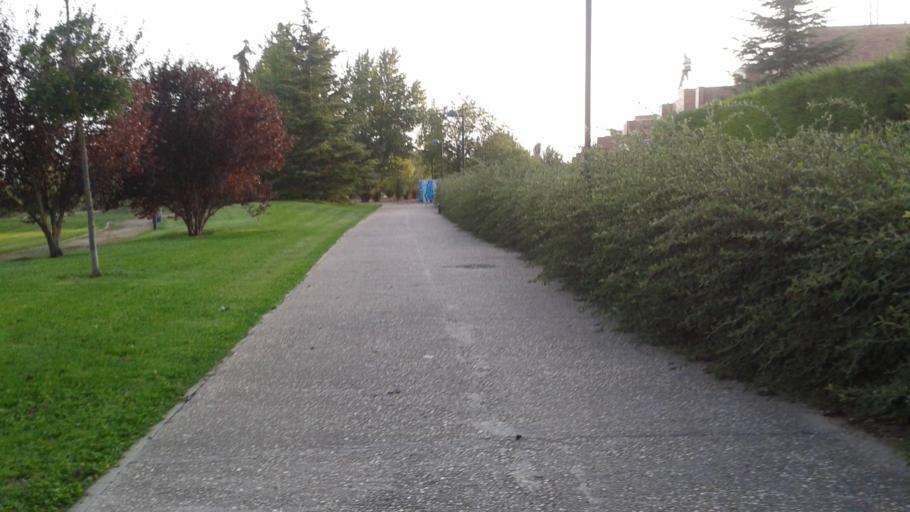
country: ES
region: Castille and Leon
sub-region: Provincia de Valladolid
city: Arroyo
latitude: 41.6141
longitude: -4.7784
